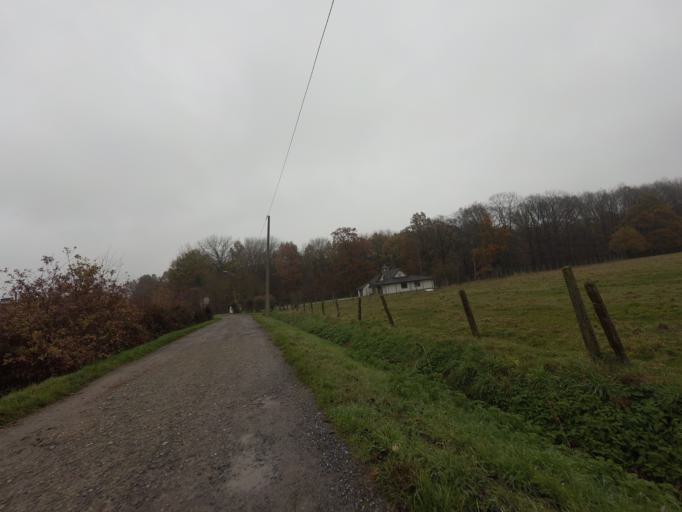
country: BE
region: Flanders
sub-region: Provincie Vlaams-Brabant
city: Herent
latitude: 50.9102
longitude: 4.6317
